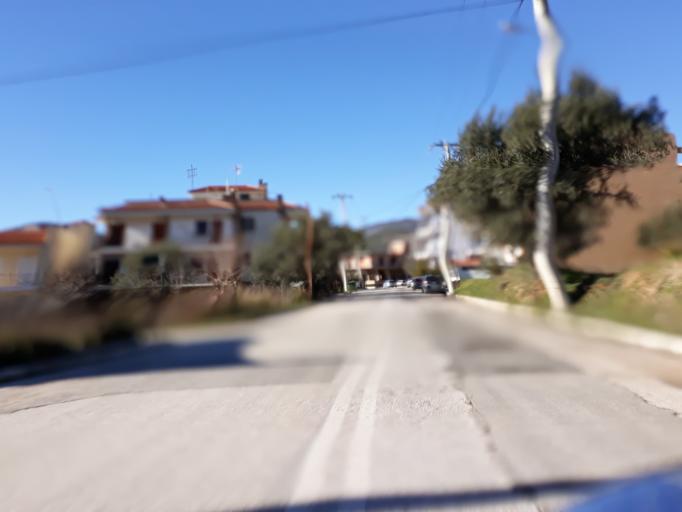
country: GR
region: Attica
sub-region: Nomarchia Dytikis Attikis
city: Fyli
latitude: 38.1083
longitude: 23.6720
